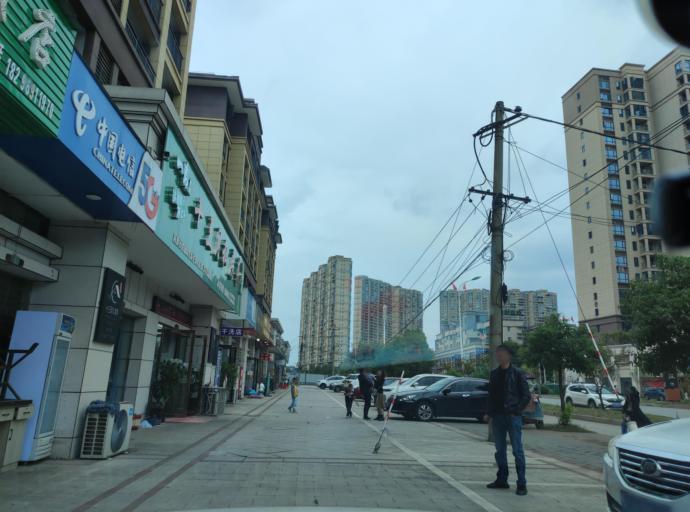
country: CN
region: Jiangxi Sheng
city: Pingxiang
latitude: 27.6757
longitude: 113.9054
